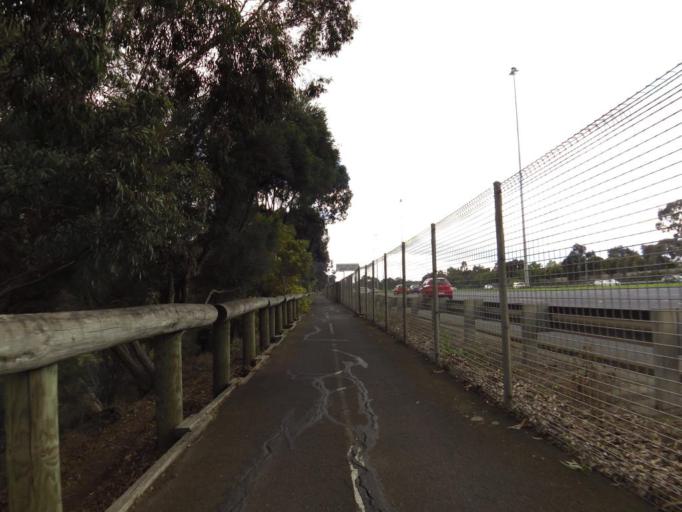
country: AU
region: Victoria
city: Ivanhoe East
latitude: -37.7883
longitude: 145.0548
